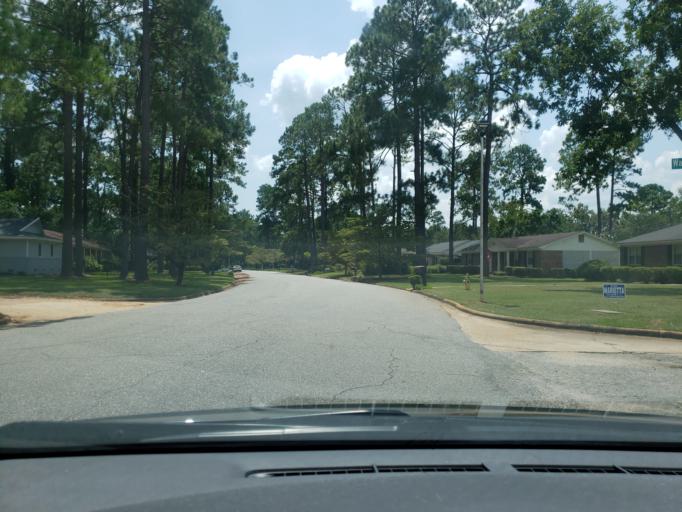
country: US
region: Georgia
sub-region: Dougherty County
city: Albany
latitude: 31.6016
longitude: -84.2051
